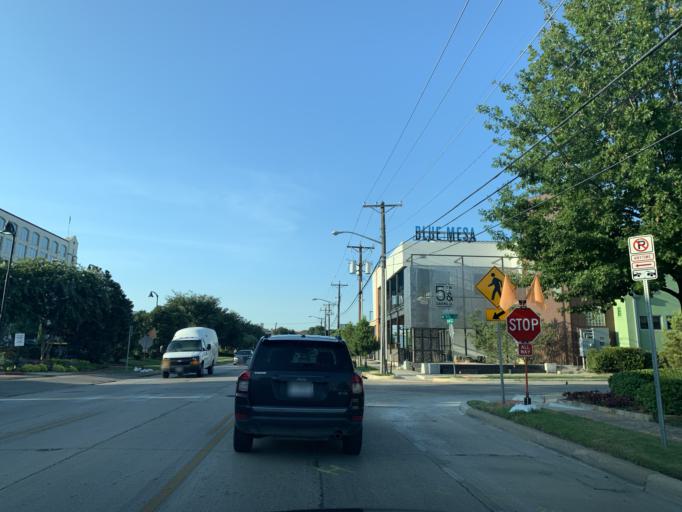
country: US
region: Texas
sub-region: Tarrant County
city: Fort Worth
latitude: 32.7532
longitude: -97.3548
